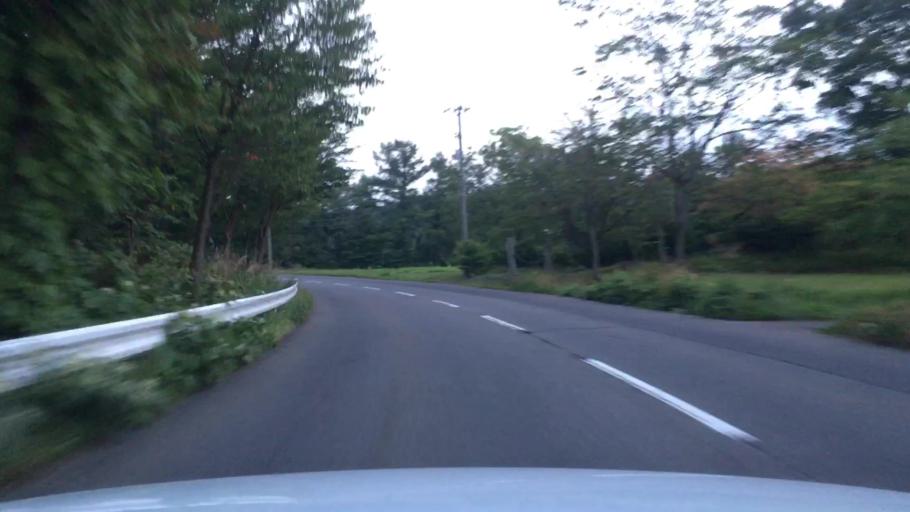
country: JP
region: Aomori
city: Shimokizukuri
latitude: 40.6879
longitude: 140.3631
